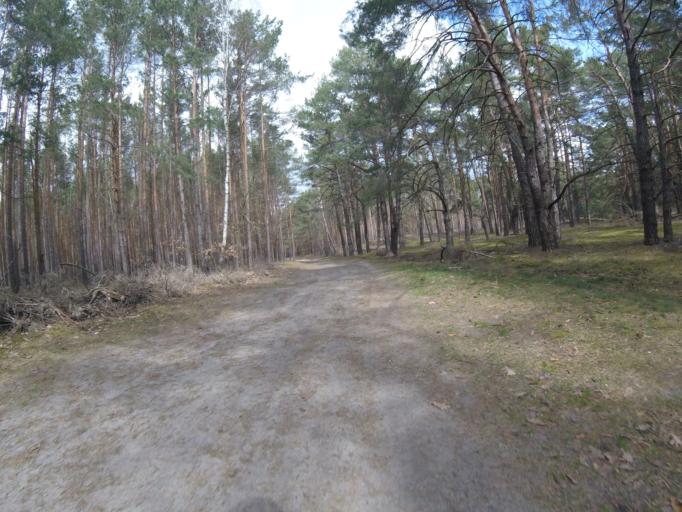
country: DE
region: Brandenburg
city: Gross Koris
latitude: 52.1865
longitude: 13.6586
